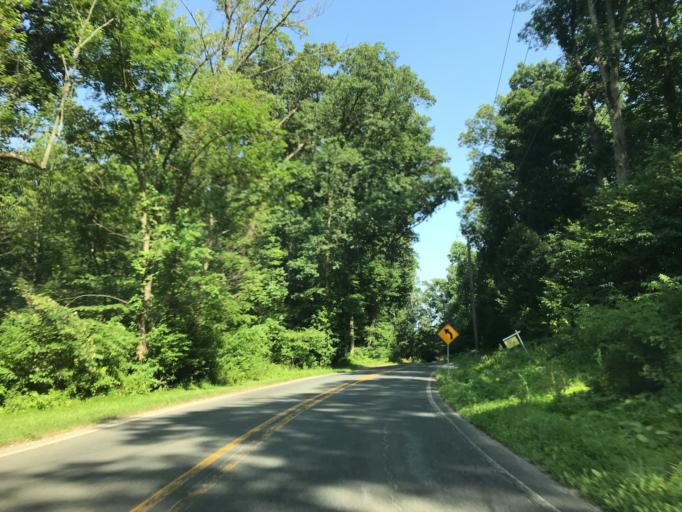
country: US
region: Maryland
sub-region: Carroll County
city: Manchester
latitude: 39.6691
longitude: -76.8588
